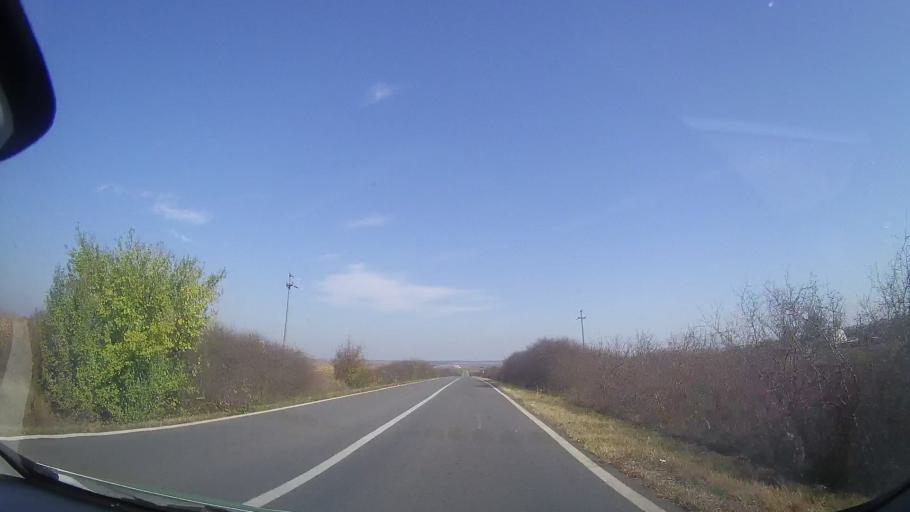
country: RO
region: Timis
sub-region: Comuna Belint
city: Belint
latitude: 45.7655
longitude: 21.7279
